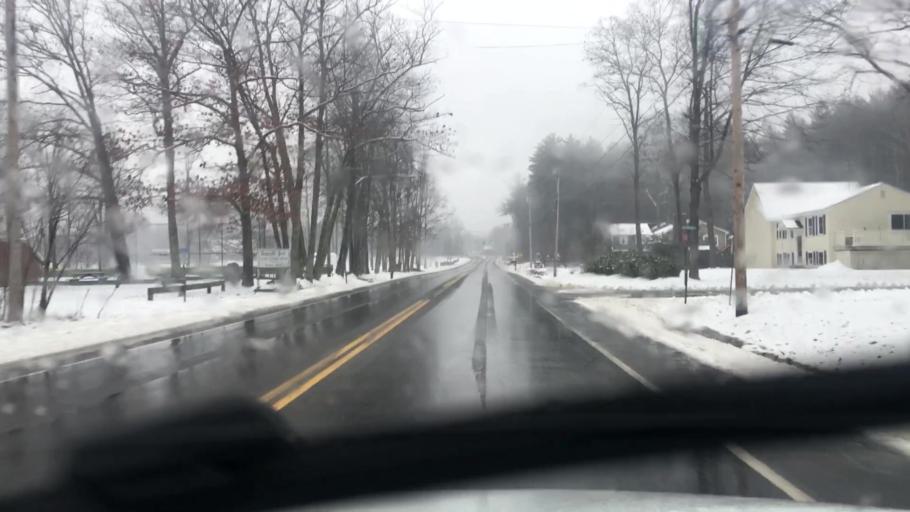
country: US
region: Maine
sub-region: York County
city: Buxton
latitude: 43.6013
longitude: -70.5354
